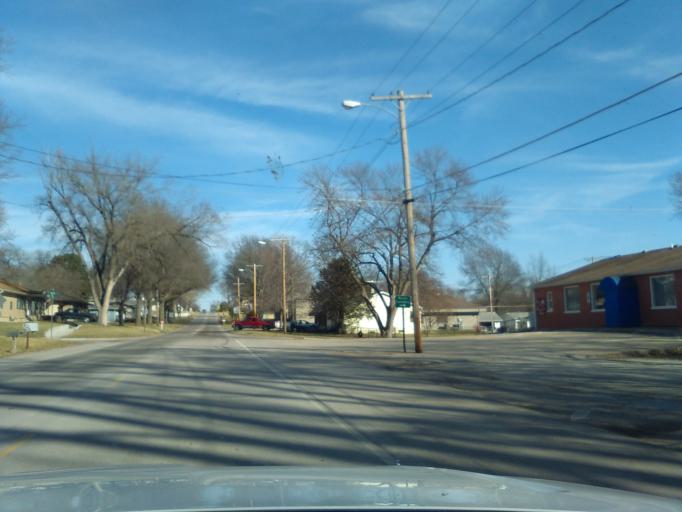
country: US
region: Nebraska
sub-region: Otoe County
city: Nebraska City
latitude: 40.6731
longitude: -95.8695
